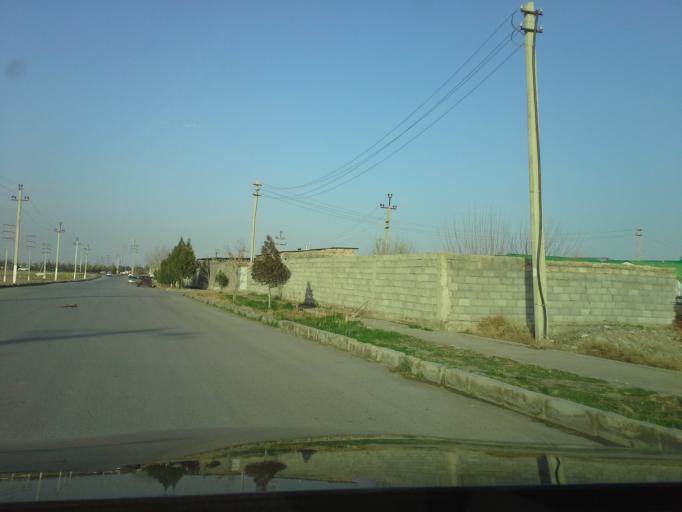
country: TM
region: Ahal
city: Abadan
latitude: 38.0293
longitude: 58.2243
